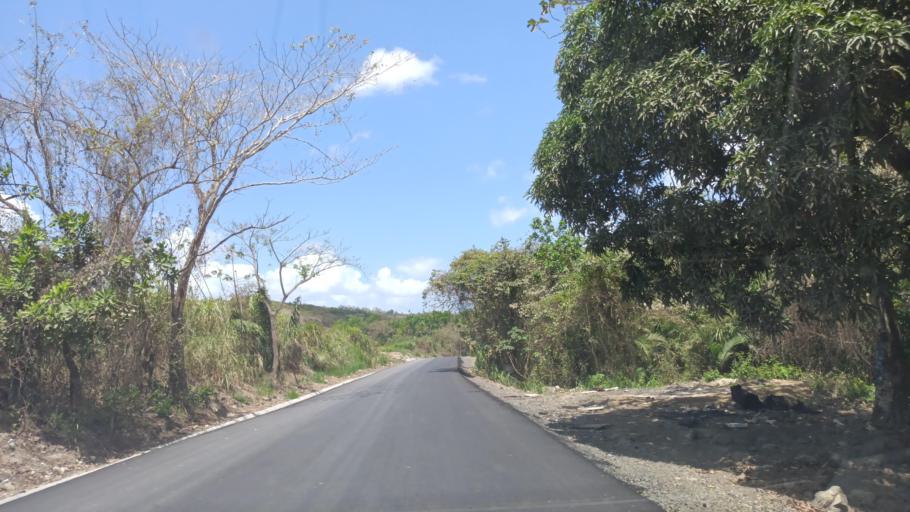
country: PA
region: Panama
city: Alcalde Diaz
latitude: 9.0903
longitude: -79.5771
